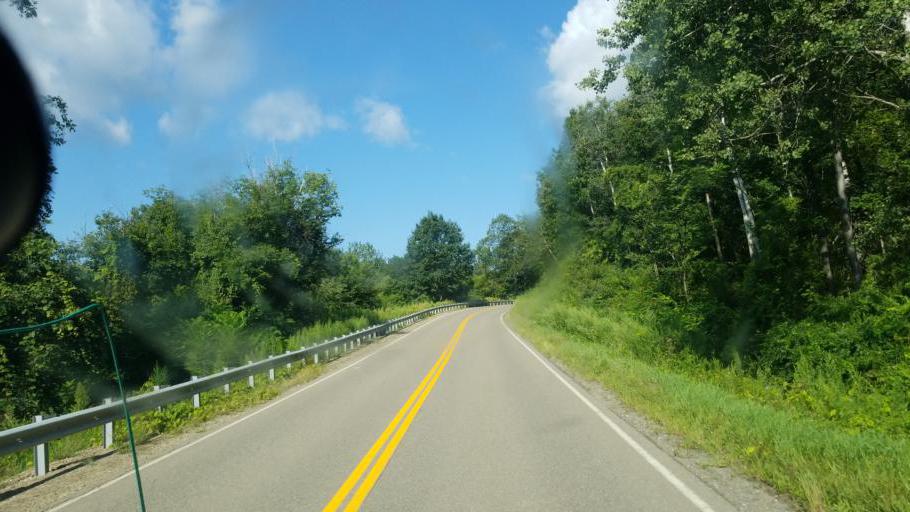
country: US
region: New York
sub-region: Steuben County
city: Canisteo
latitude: 42.2663
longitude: -77.5837
